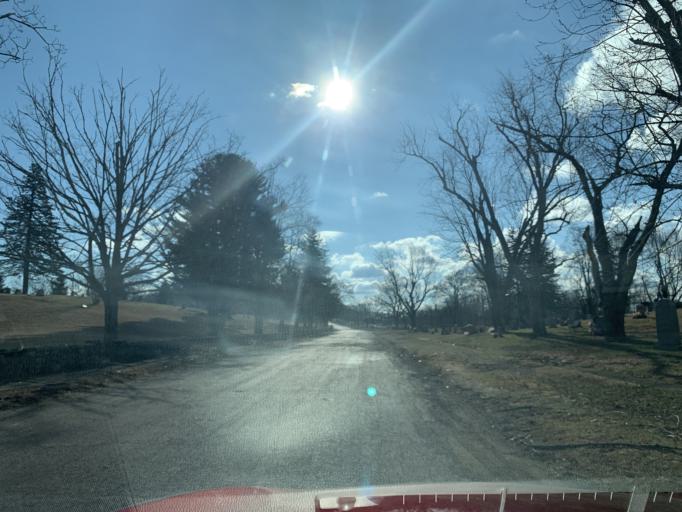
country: US
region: Massachusetts
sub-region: Essex County
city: Amesbury
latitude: 42.8459
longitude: -70.9347
